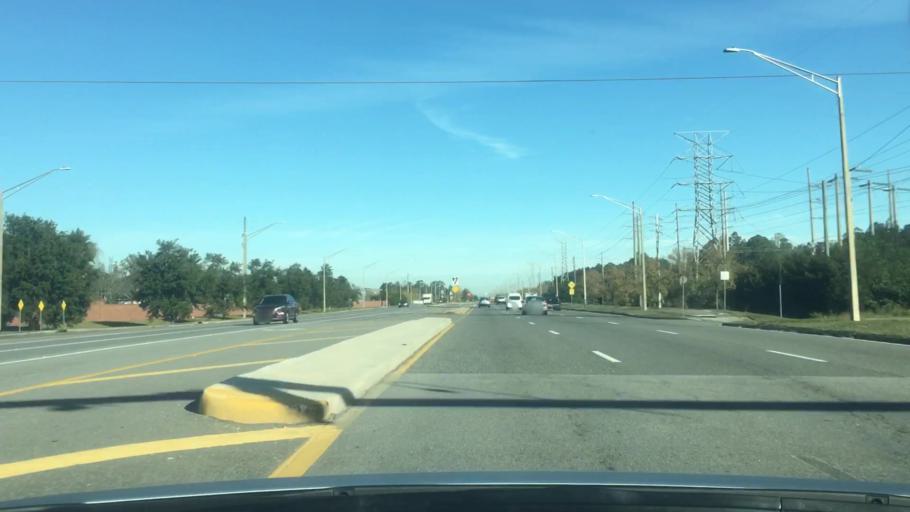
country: US
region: Florida
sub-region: Duval County
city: Neptune Beach
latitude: 30.2955
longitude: -81.4889
